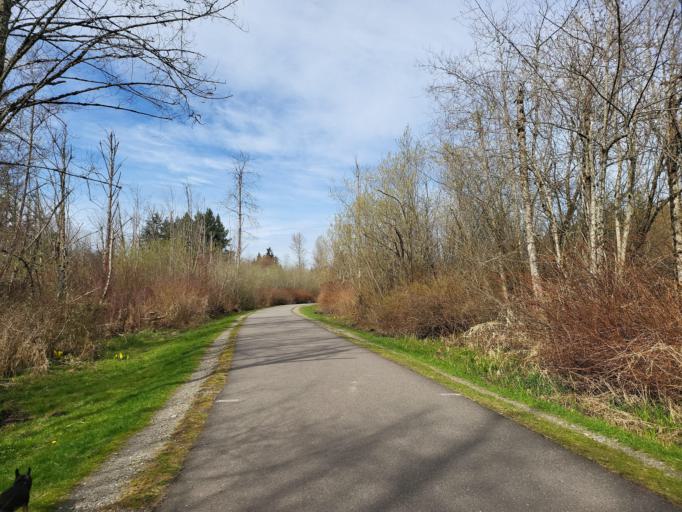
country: US
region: Washington
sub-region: King County
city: East Hill-Meridian
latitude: 47.4097
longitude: -122.1594
